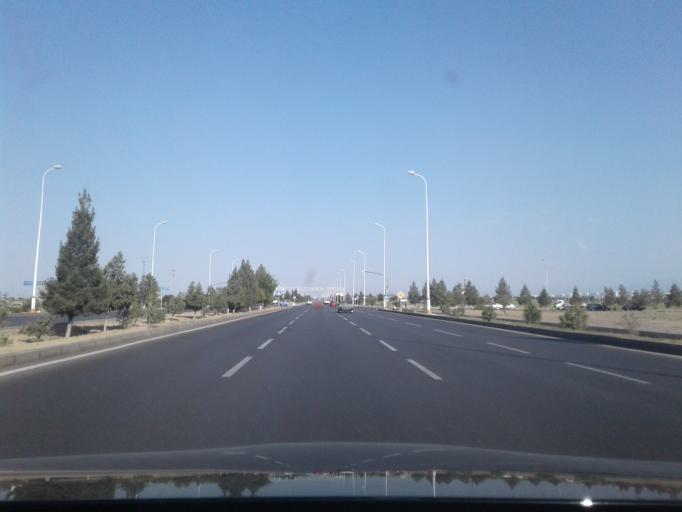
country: TM
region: Ahal
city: Ashgabat
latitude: 38.0012
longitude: 58.2977
